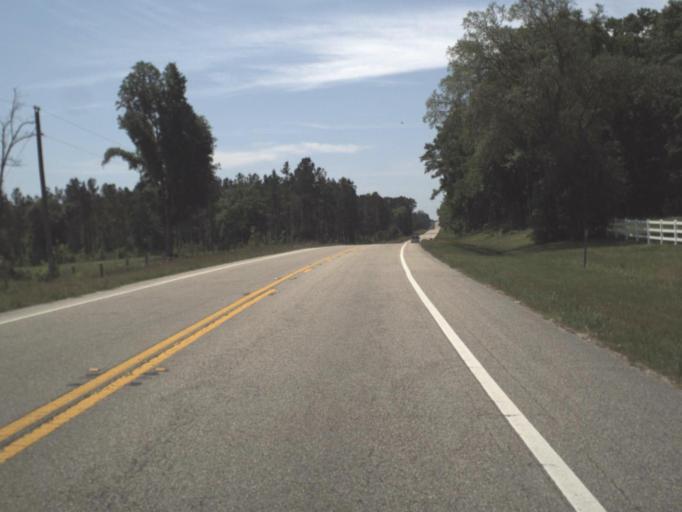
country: US
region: Florida
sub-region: Jackson County
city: Marianna
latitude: 30.6208
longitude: -85.1807
